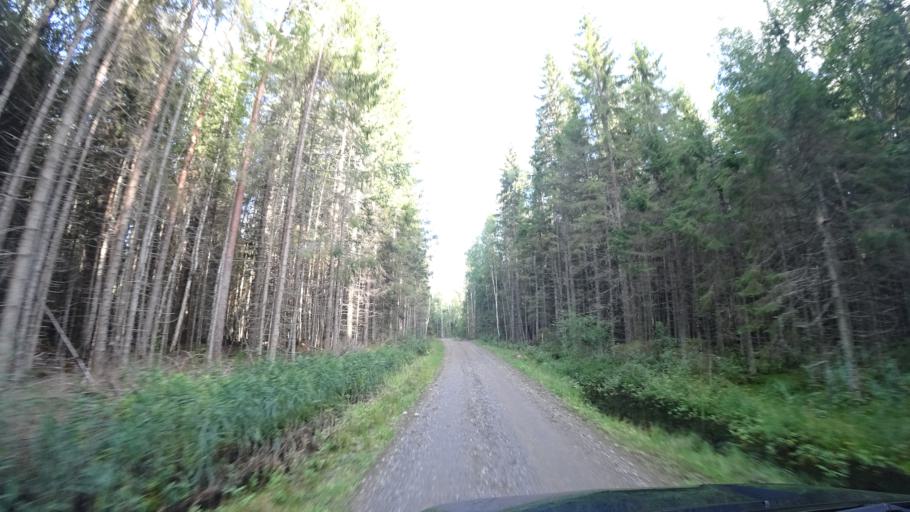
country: FI
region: Paijanne Tavastia
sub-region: Lahti
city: Auttoinen
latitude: 61.2195
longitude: 25.2069
